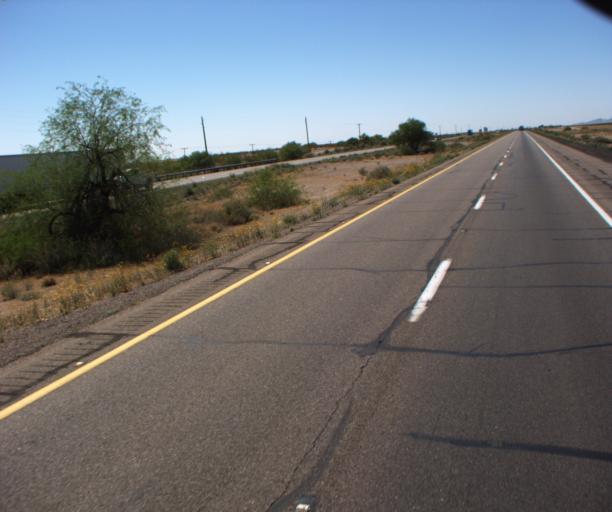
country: US
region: Arizona
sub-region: Maricopa County
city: Gila Bend
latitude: 32.9355
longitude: -112.7812
